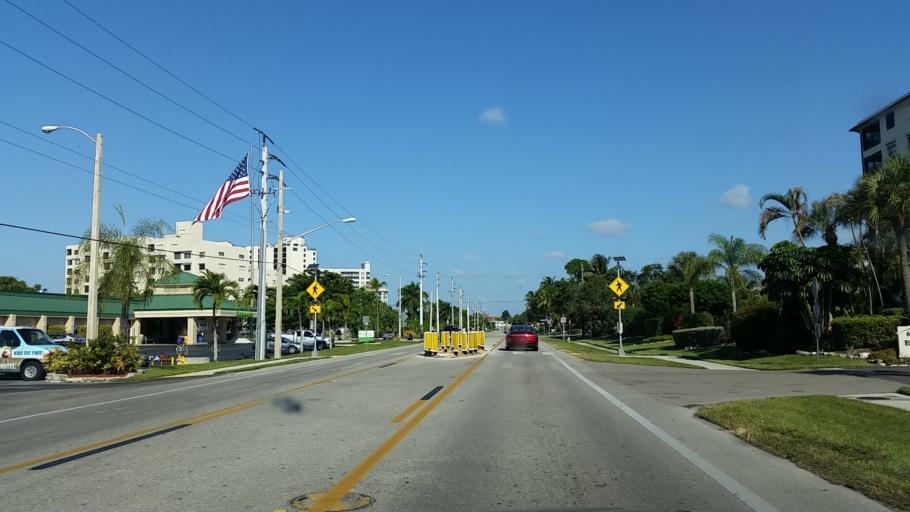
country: US
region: Florida
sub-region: Lee County
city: Fort Myers Beach
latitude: 26.4163
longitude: -81.9014
